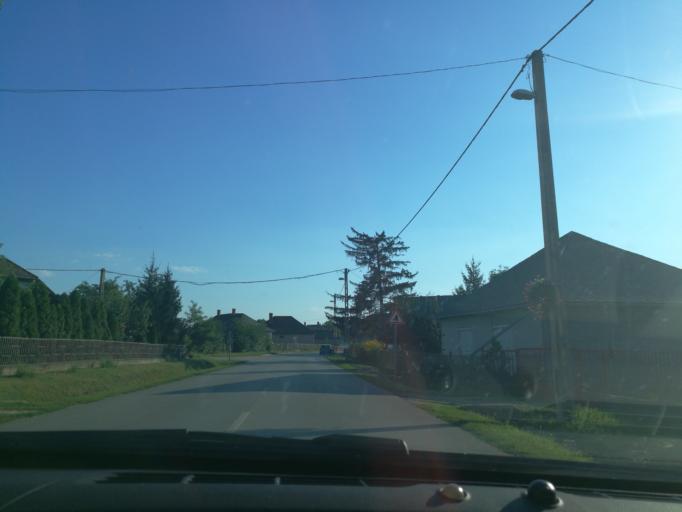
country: HU
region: Szabolcs-Szatmar-Bereg
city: Buj
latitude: 48.1012
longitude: 21.6505
